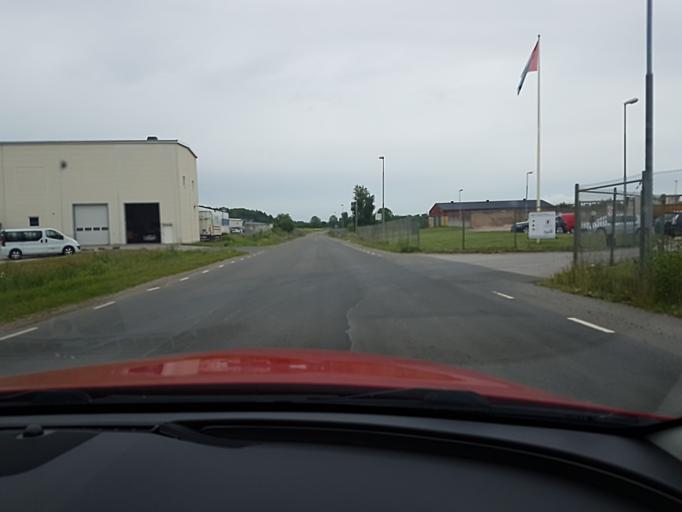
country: SE
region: Vaestra Goetaland
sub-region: Skovde Kommun
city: Skoevde
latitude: 58.3864
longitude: 13.8831
